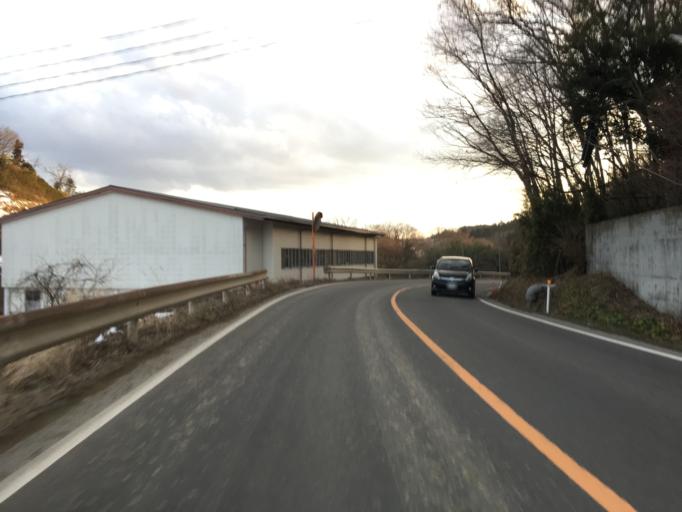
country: JP
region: Fukushima
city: Fukushima-shi
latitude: 37.6624
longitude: 140.5132
